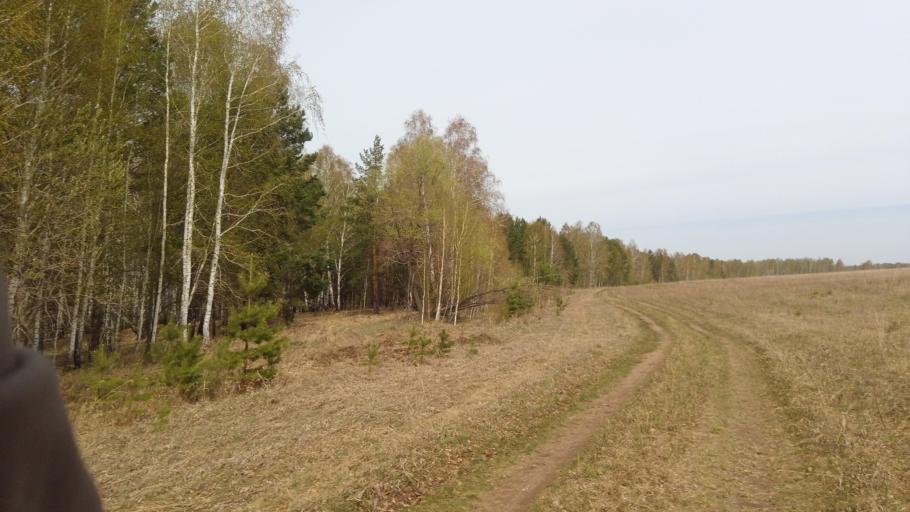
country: RU
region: Chelyabinsk
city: Timiryazevskiy
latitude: 55.0168
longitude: 60.8616
